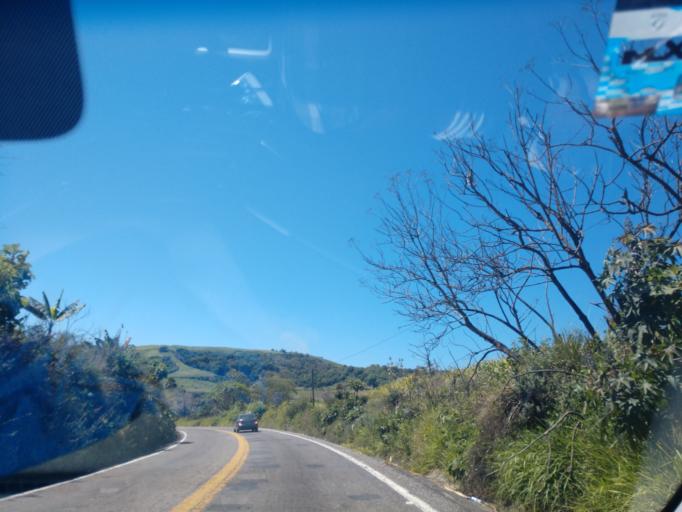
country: MX
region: Nayarit
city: Xalisco
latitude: 21.3688
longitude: -104.9141
